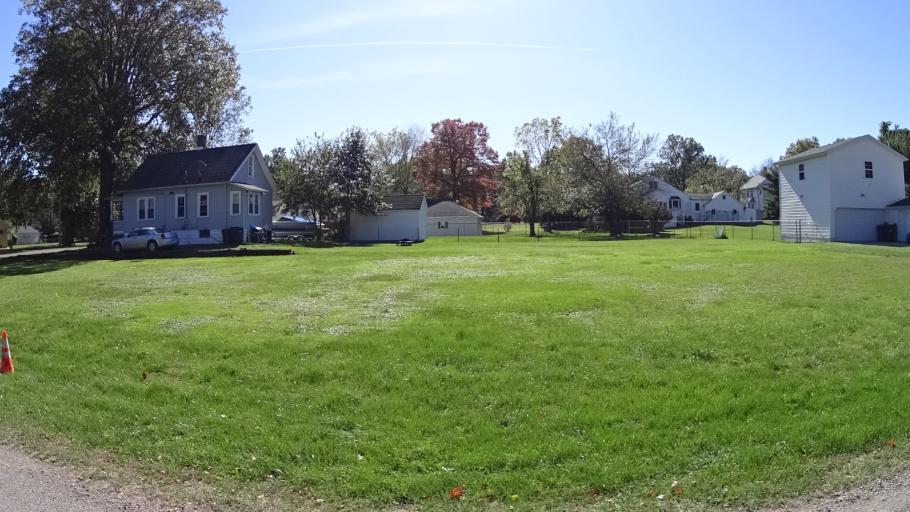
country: US
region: Ohio
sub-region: Lorain County
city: Lorain
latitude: 41.4291
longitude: -82.1588
